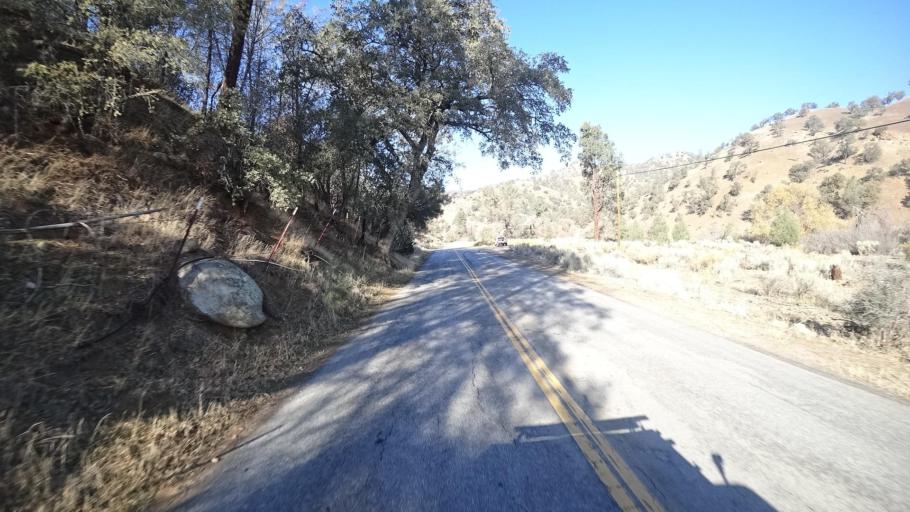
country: US
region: California
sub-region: Kern County
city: Golden Hills
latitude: 35.3050
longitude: -118.4393
